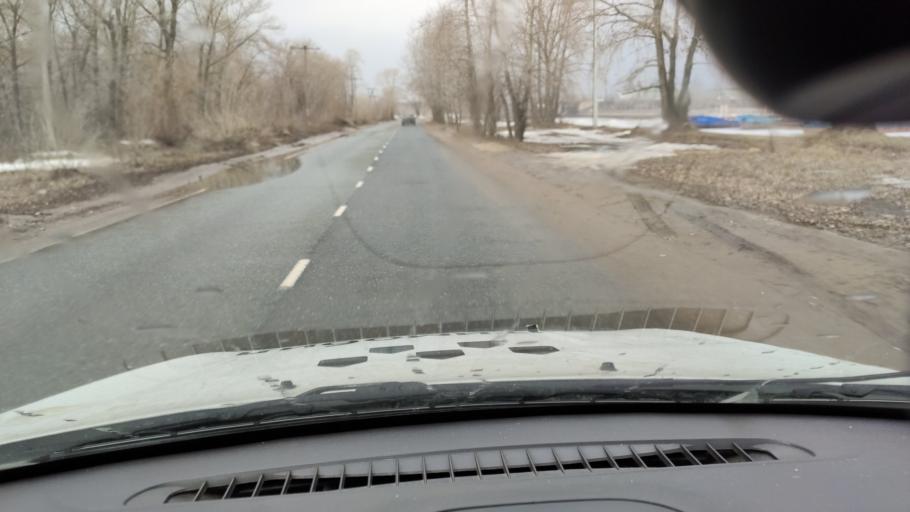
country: RU
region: Samara
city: Zhigulevsk
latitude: 53.4600
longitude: 49.5208
